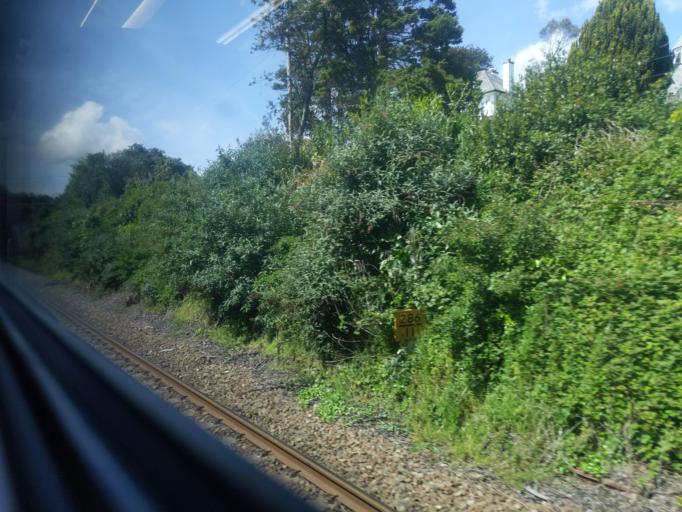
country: GB
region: England
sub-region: Cornwall
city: St Austell
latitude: 50.3402
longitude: -4.7921
